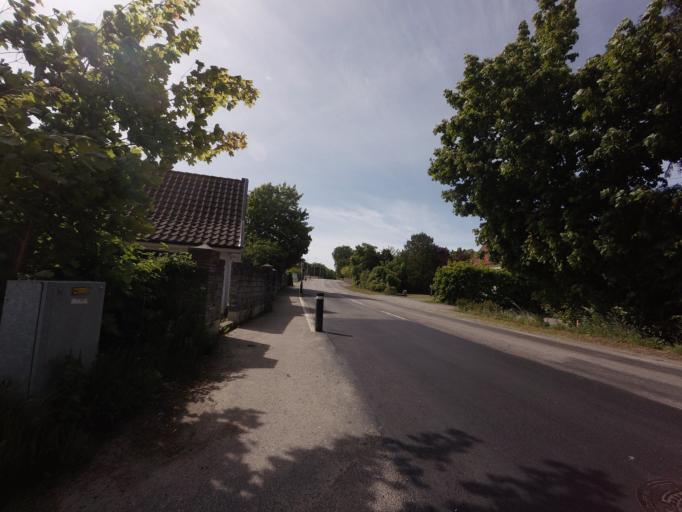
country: SE
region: Skane
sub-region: Helsingborg
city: Odakra
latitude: 56.1271
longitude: 12.6943
